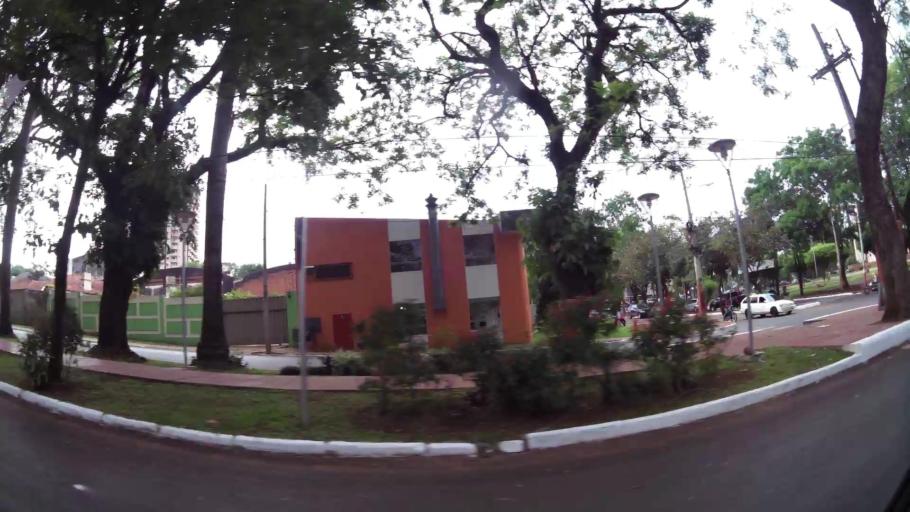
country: PY
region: Alto Parana
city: Ciudad del Este
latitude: -25.5187
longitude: -54.6087
